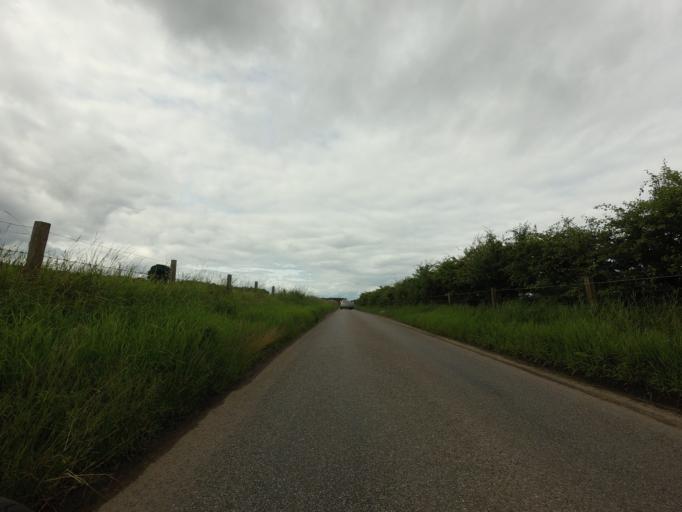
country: GB
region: Scotland
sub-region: Moray
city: Forres
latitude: 57.6226
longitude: -3.6699
